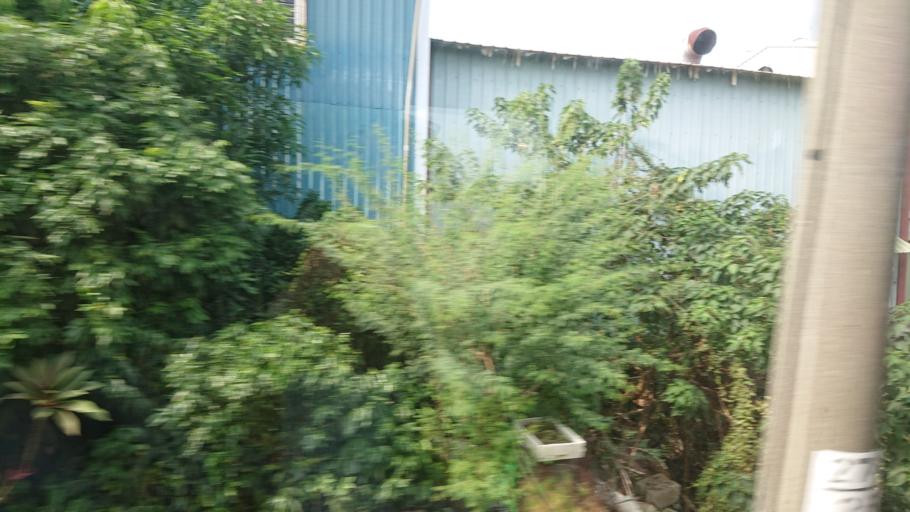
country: TW
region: Taiwan
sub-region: Yunlin
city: Douliu
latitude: 23.6599
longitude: 120.4742
